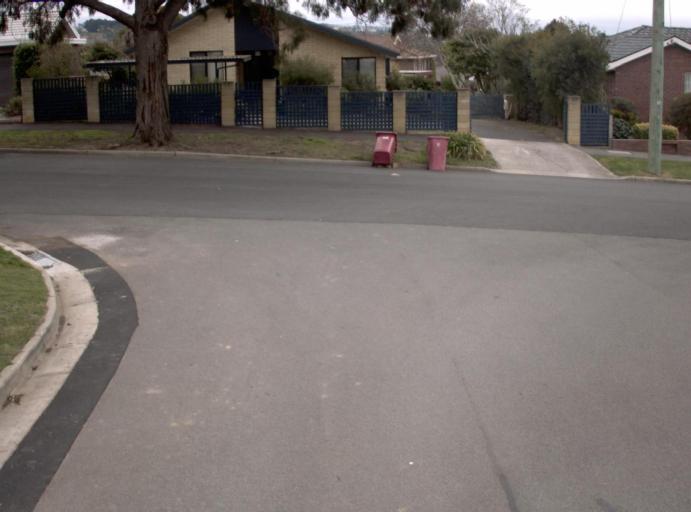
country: AU
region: Tasmania
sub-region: Launceston
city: Newstead
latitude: -41.4590
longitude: 147.1783
